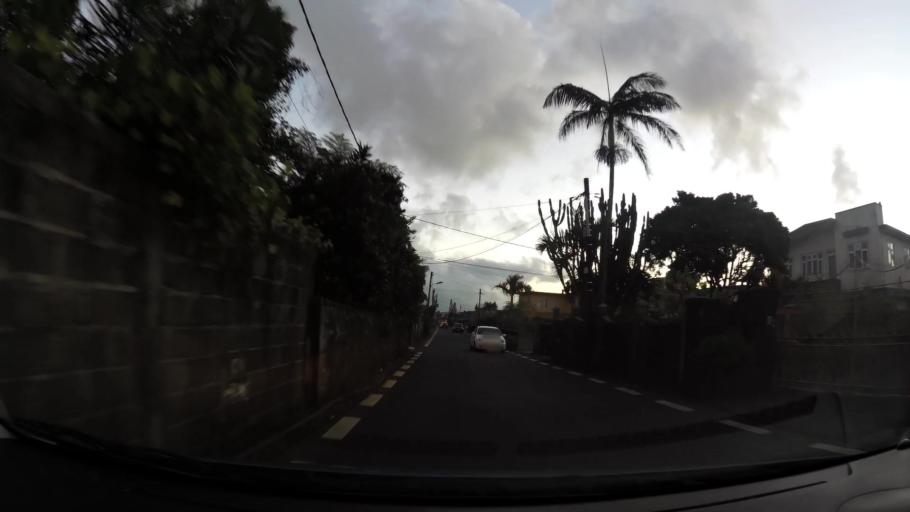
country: MU
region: Plaines Wilhems
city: Curepipe
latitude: -20.2902
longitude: 57.5237
